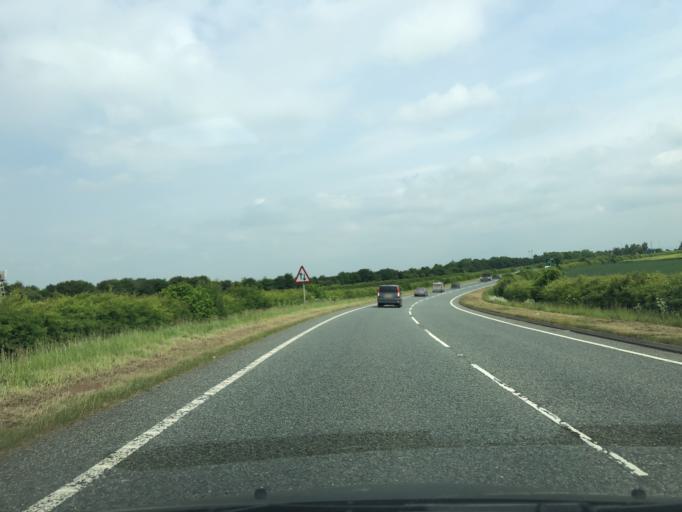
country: GB
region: England
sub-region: North Yorkshire
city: Boroughbridge
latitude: 54.1494
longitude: -1.4330
